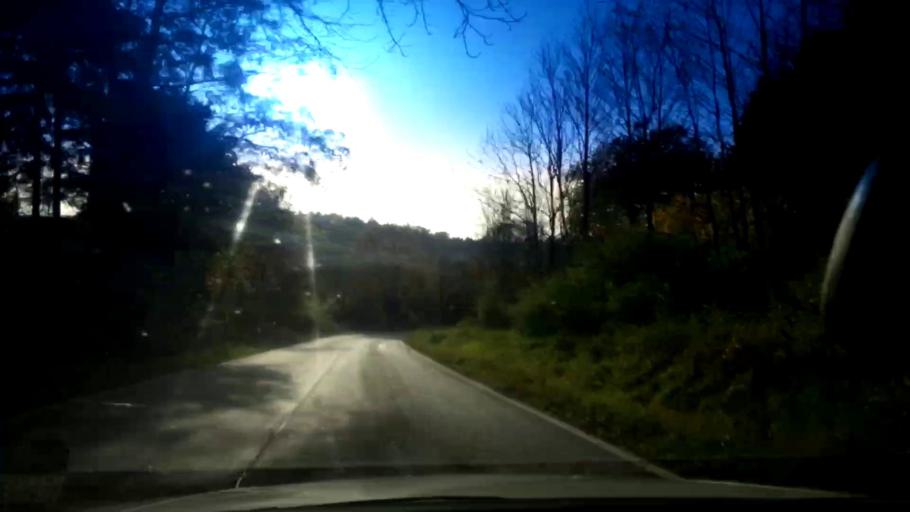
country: DE
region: Bavaria
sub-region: Upper Franconia
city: Poxdorf
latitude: 49.9509
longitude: 11.0828
